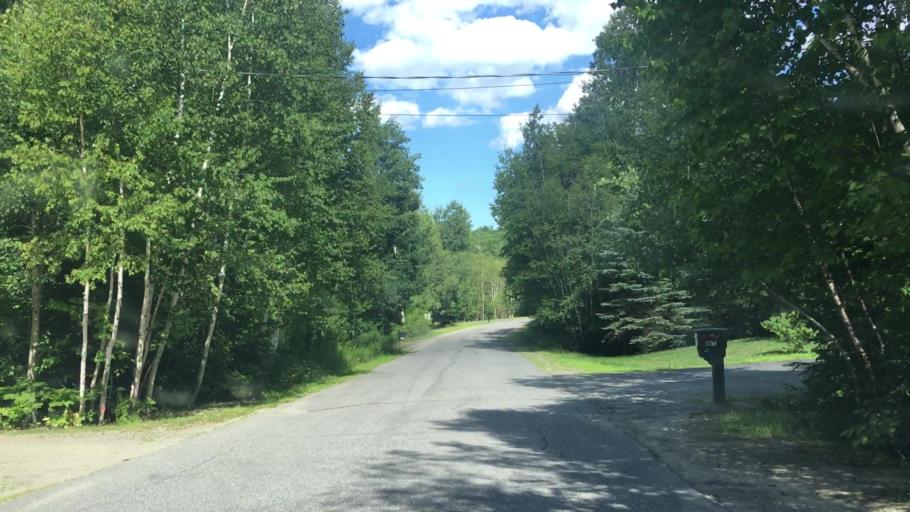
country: US
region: Maine
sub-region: Franklin County
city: Farmington
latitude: 44.6716
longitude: -70.1329
